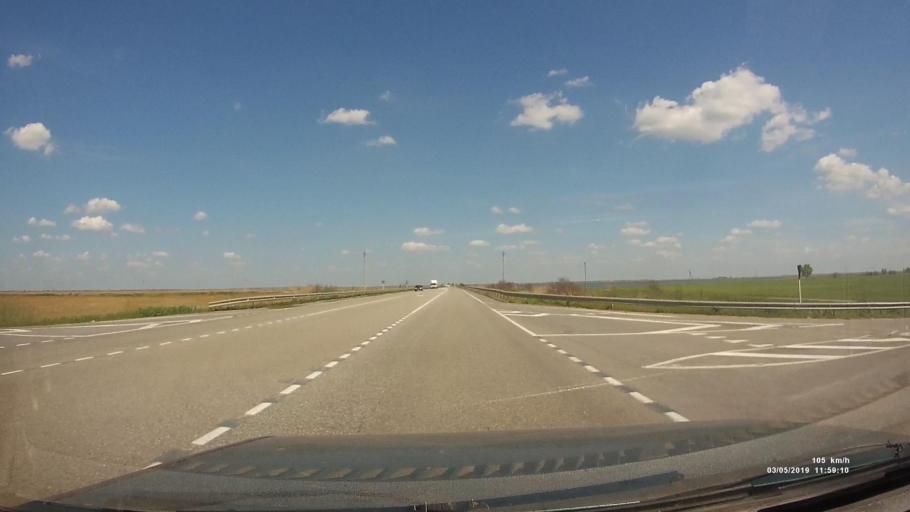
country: RU
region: Rostov
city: Bagayevskaya
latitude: 47.2311
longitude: 40.3276
